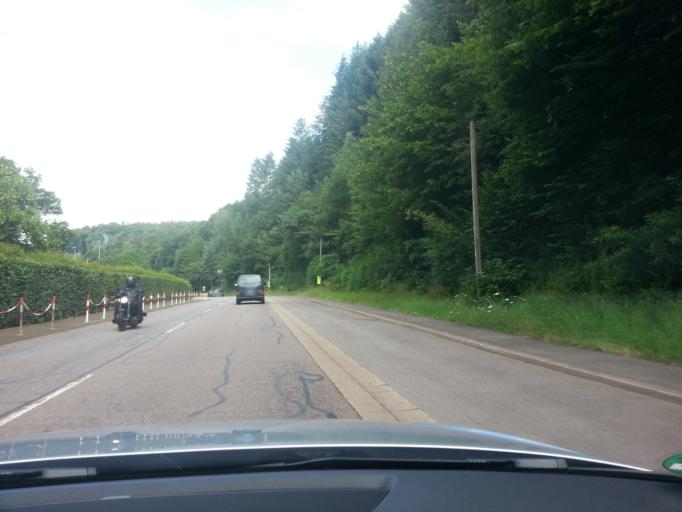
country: DE
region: Saarland
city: Mettlach
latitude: 49.4918
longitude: 6.6249
